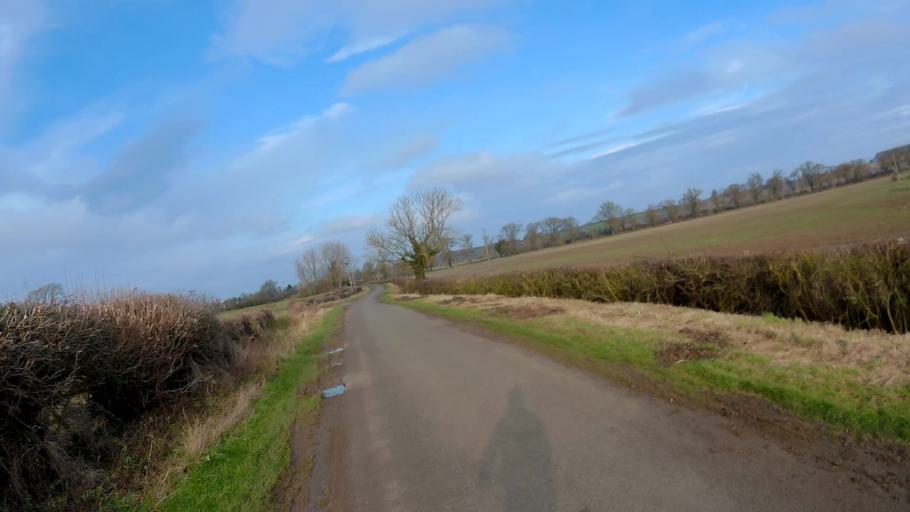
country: GB
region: England
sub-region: Lincolnshire
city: Bourne
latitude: 52.7735
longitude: -0.4259
